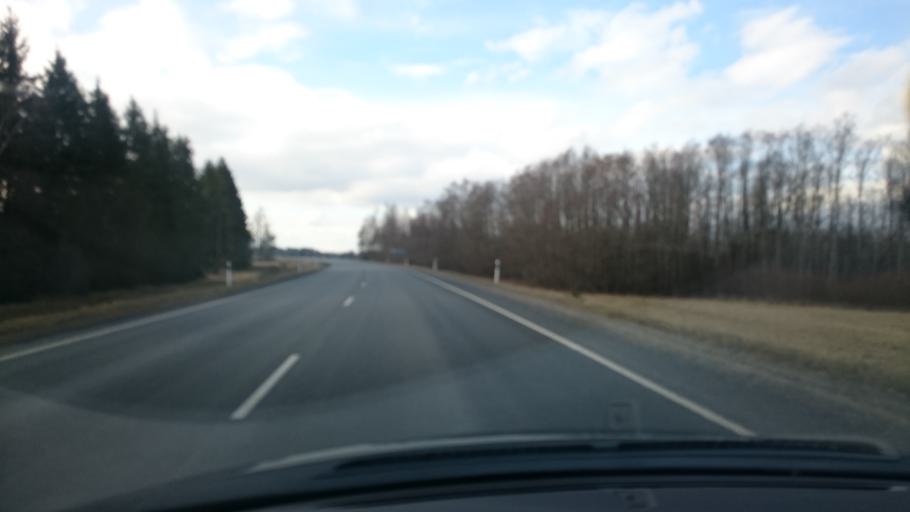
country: EE
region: Harju
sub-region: Nissi vald
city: Turba
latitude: 58.9246
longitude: 24.1110
